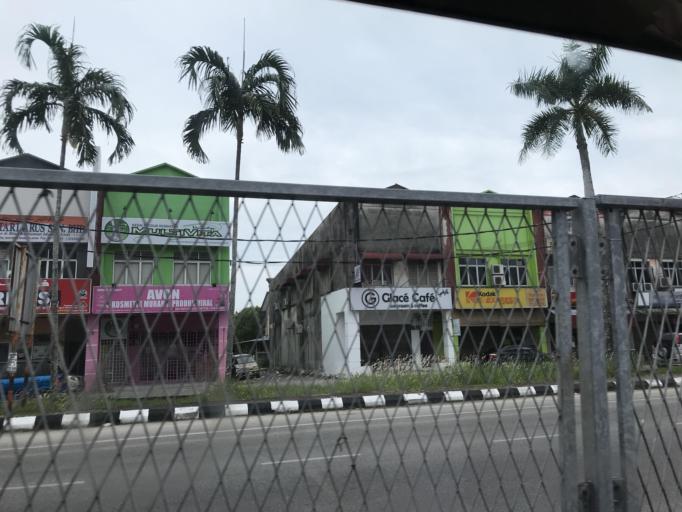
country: MY
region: Kelantan
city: Kota Bharu
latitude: 6.1144
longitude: 102.2143
